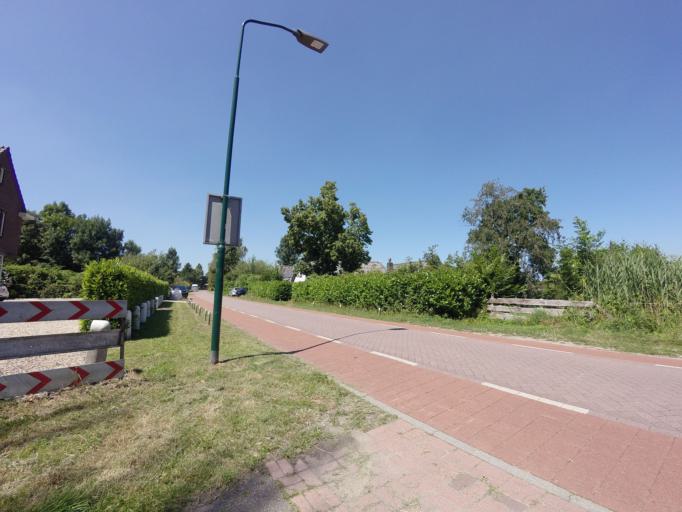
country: NL
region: Utrecht
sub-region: Stichtse Vecht
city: Maarssen
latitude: 52.1451
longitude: 5.0886
